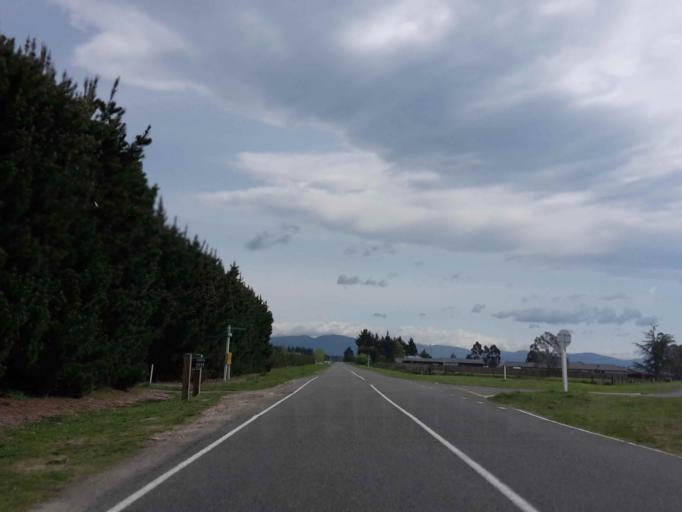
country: NZ
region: Canterbury
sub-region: Waimakariri District
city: Kaiapoi
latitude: -43.3773
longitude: 172.5319
